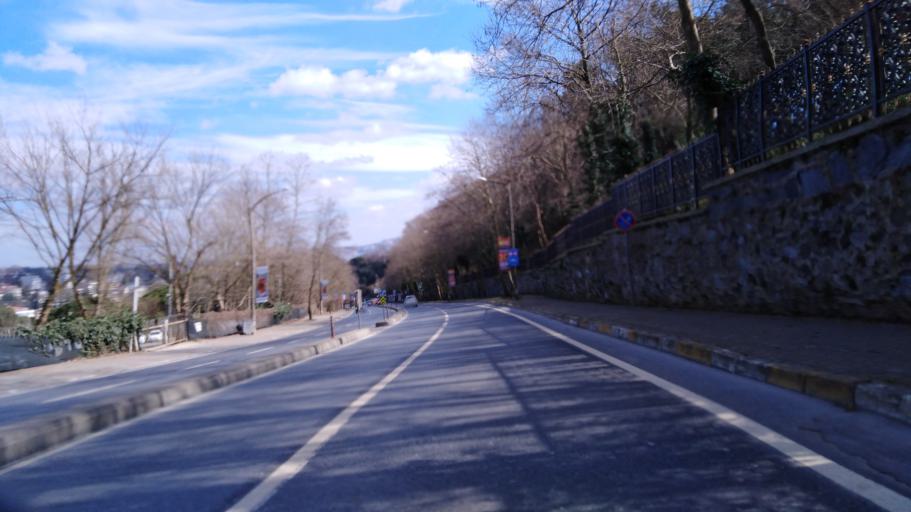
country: TR
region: Istanbul
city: Sisli
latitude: 41.1106
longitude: 29.0513
